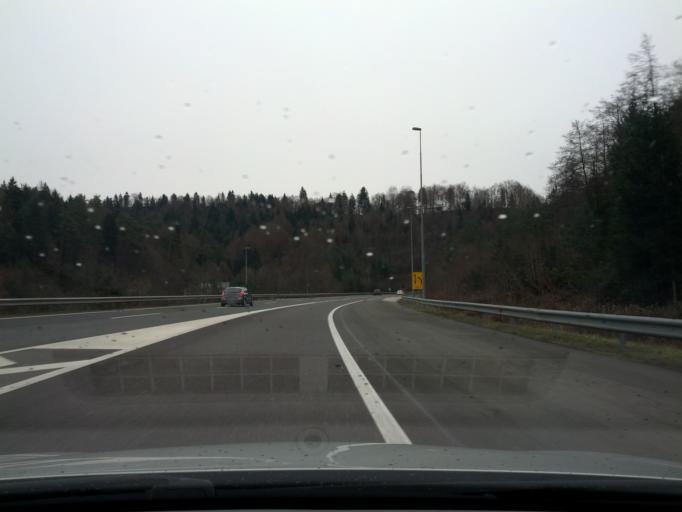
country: SI
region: Skofljica
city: Lavrica
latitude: 46.0123
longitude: 14.5603
